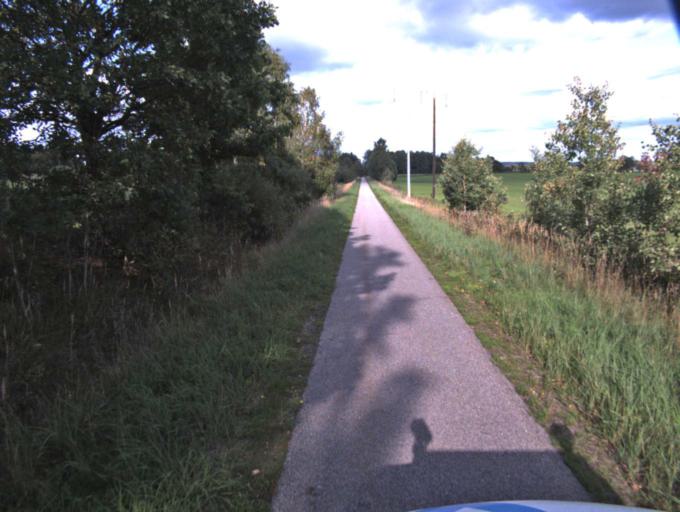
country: SE
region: Vaestra Goetaland
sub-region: Ulricehamns Kommun
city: Ulricehamn
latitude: 57.8935
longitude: 13.4414
